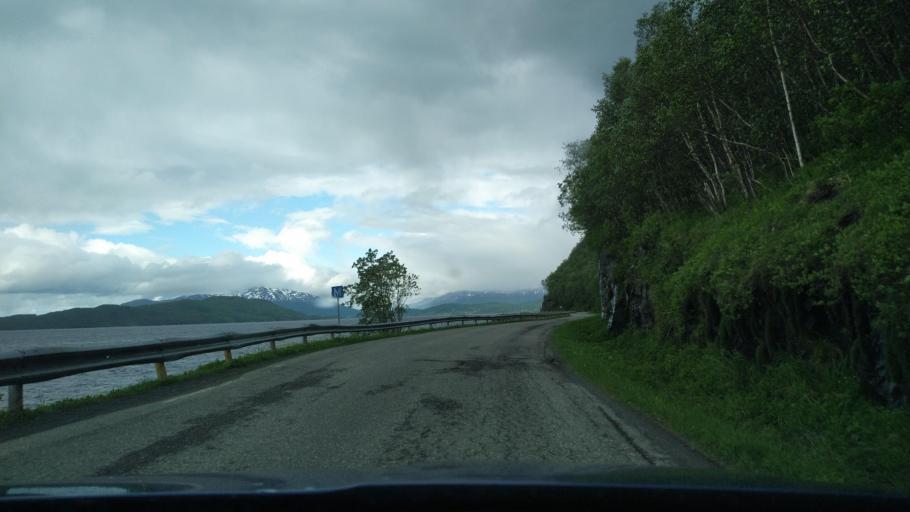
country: NO
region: Troms
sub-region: Lenvik
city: Finnsnes
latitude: 69.1418
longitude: 17.9150
